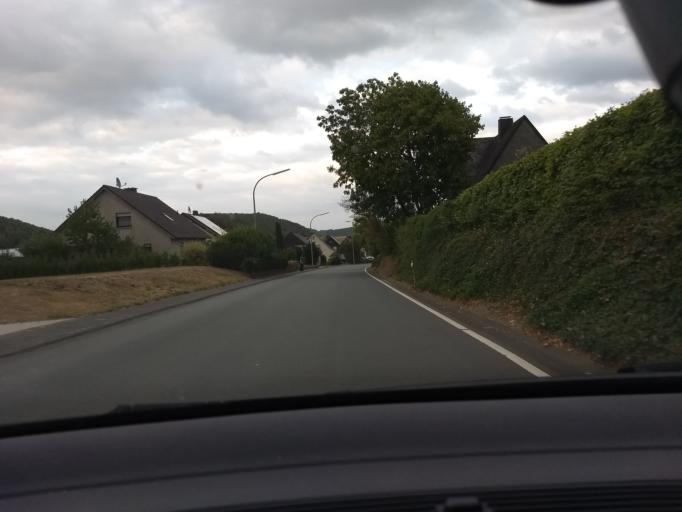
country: DE
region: North Rhine-Westphalia
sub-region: Regierungsbezirk Arnsberg
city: Arnsberg
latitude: 51.3324
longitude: 8.1343
